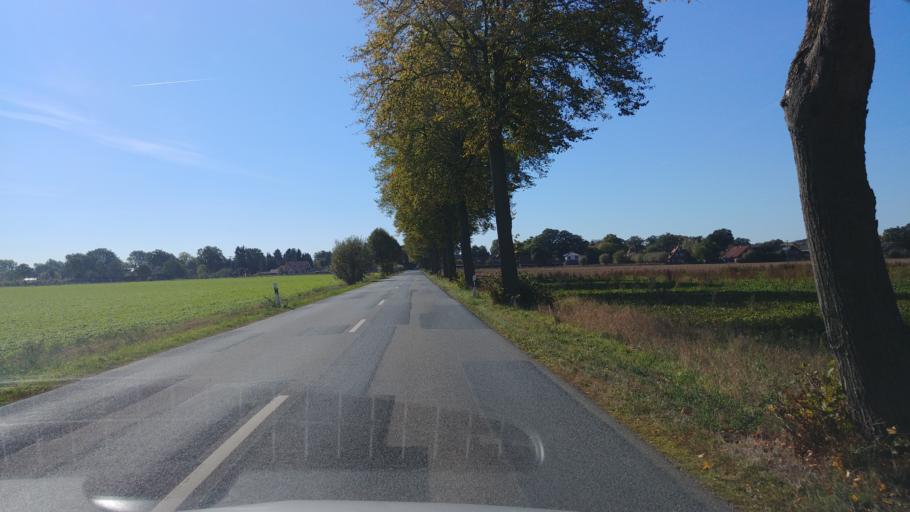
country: DE
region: Lower Saxony
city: Meinersen
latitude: 52.4911
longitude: 10.3444
